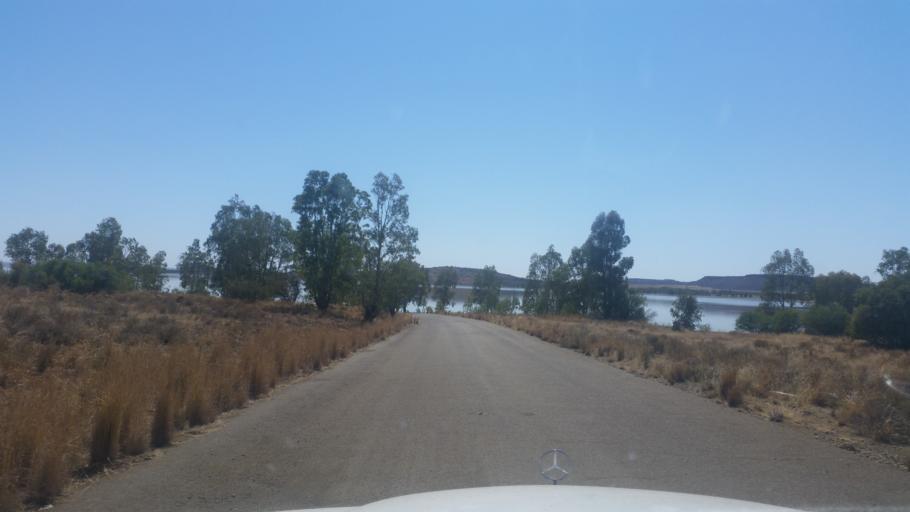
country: ZA
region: Eastern Cape
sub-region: Joe Gqabi District Municipality
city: Burgersdorp
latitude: -30.6934
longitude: 25.7791
